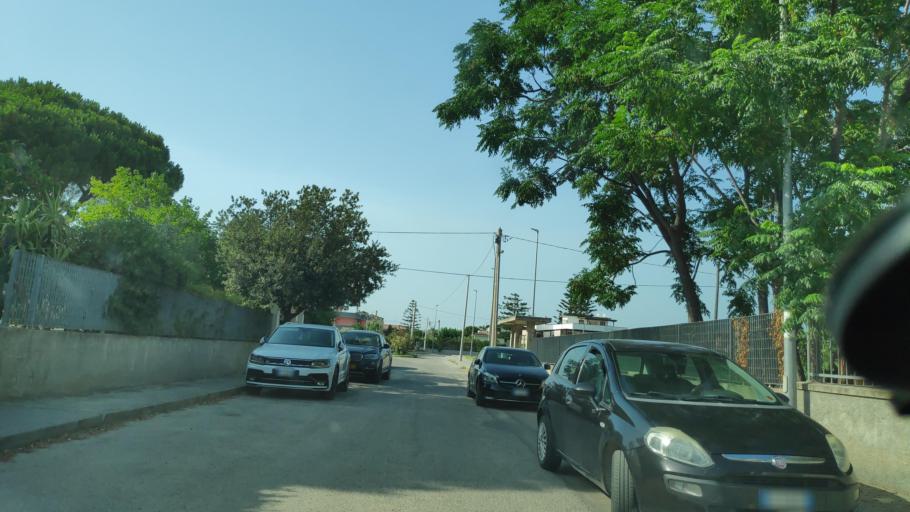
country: IT
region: Calabria
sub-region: Provincia di Catanzaro
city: Isca Marina
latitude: 38.6009
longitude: 16.5645
